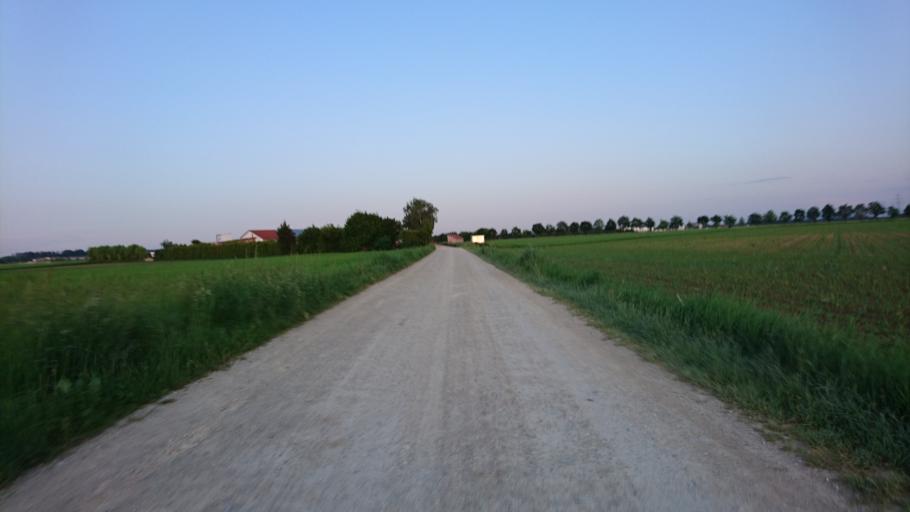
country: DE
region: Bavaria
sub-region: Upper Bavaria
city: Pliening
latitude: 48.1817
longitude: 11.7815
